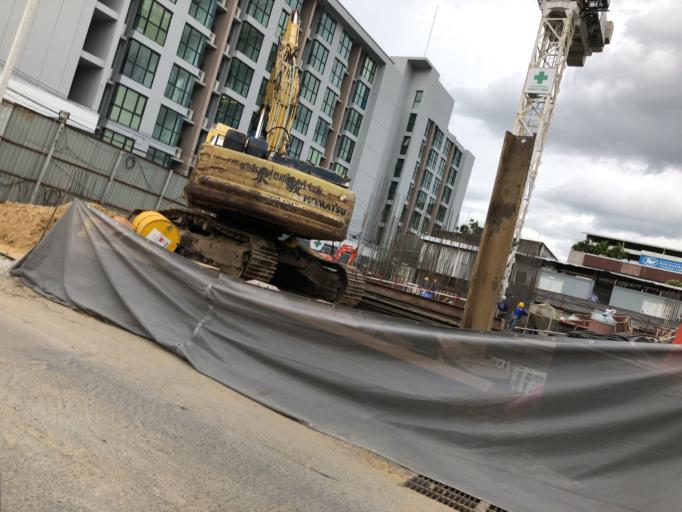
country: TH
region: Bangkok
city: Khlong Toei
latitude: 13.7168
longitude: 100.5762
